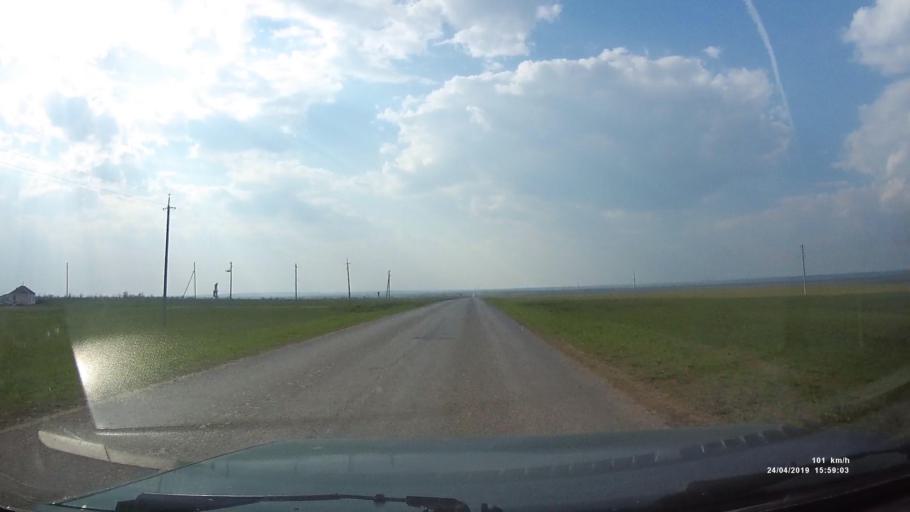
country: RU
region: Kalmykiya
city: Yashalta
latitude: 46.6199
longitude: 42.4789
